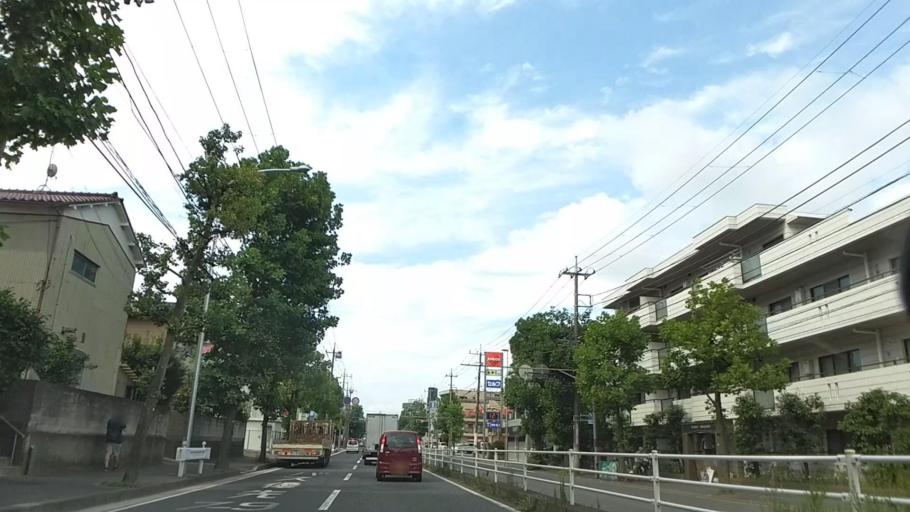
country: JP
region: Kanagawa
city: Yokohama
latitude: 35.5230
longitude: 139.6394
